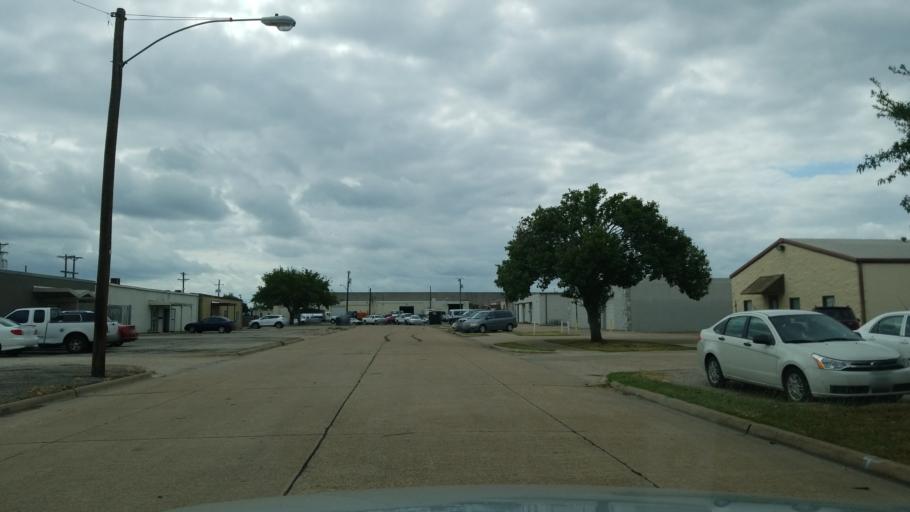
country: US
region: Texas
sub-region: Dallas County
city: Garland
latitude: 32.8843
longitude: -96.6735
